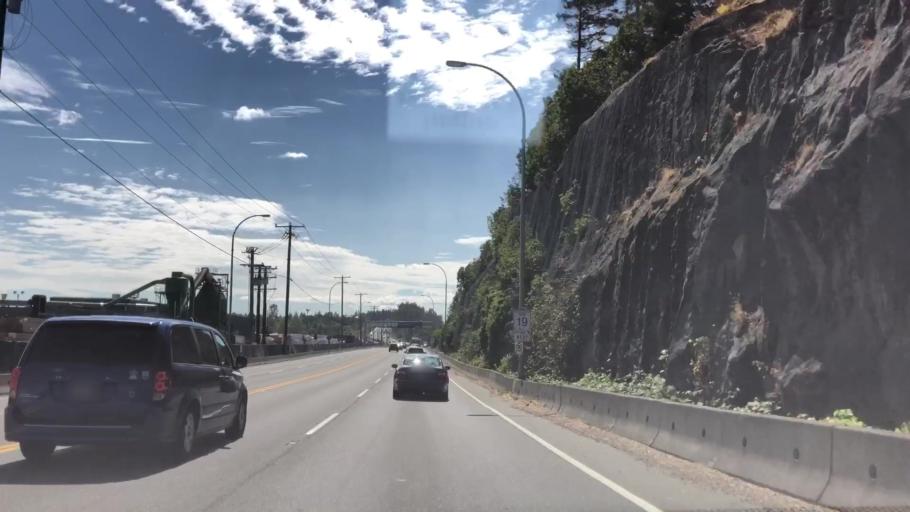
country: CA
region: British Columbia
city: Nanaimo
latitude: 49.1551
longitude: -123.8907
